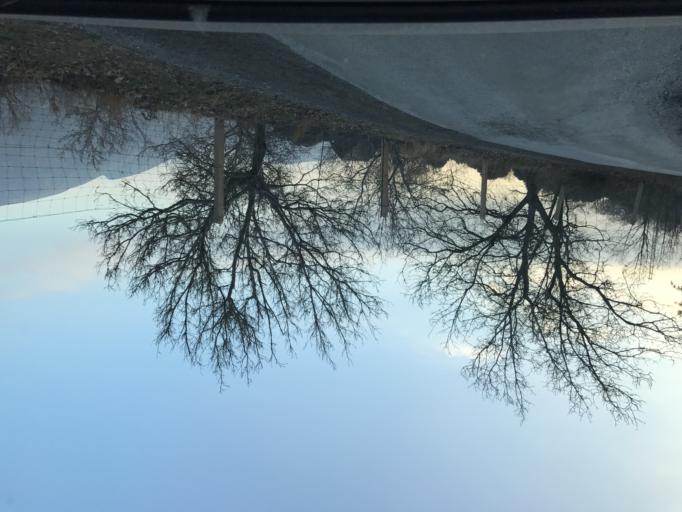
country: ES
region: Andalusia
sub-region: Provincia de Granada
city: Guejar-Sierra
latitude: 37.1370
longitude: -3.4191
